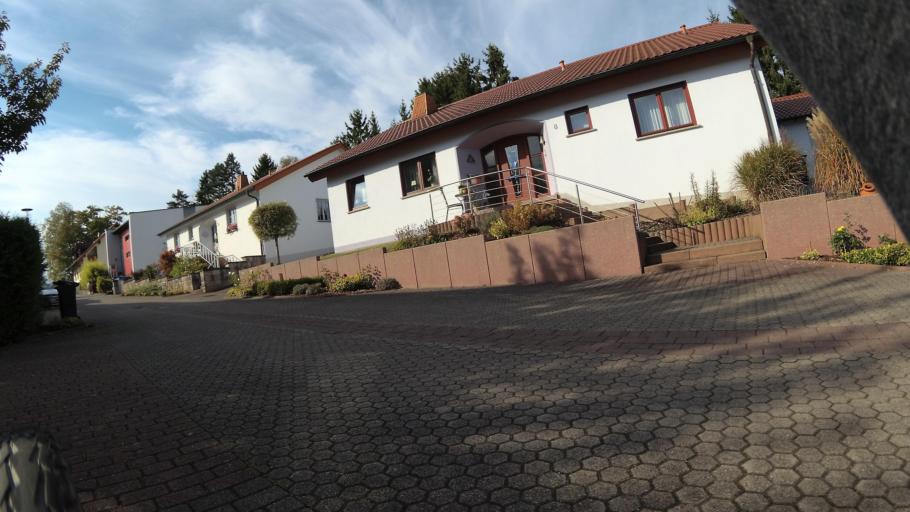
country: DE
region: Saarland
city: Schiffweiler
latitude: 49.3556
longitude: 7.1126
